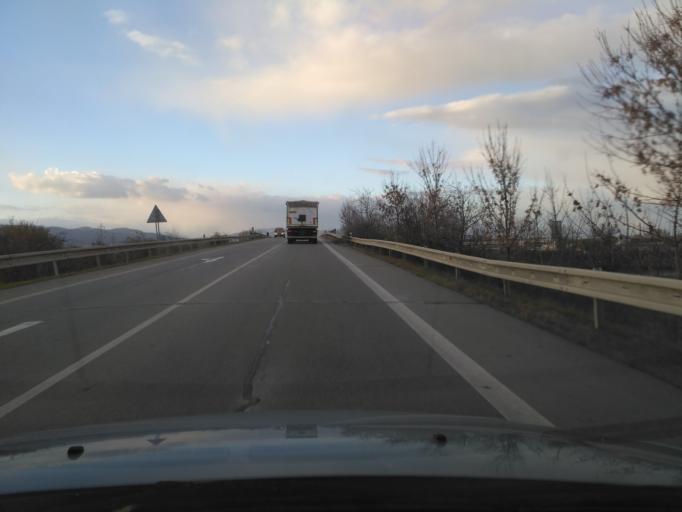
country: SK
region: Kosicky
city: Trebisov
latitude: 48.6244
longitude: 21.6987
